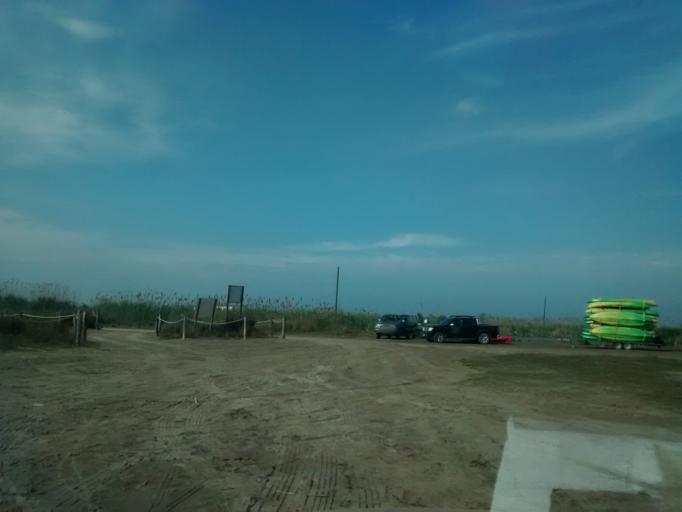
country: ES
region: Catalonia
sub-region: Provincia de Tarragona
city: Deltebre
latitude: 40.6845
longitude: 0.8530
